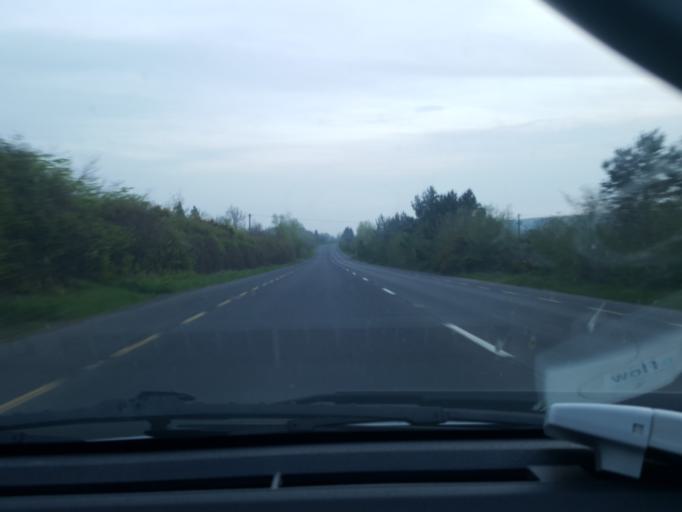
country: IE
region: Munster
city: Cahir
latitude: 52.3611
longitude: -7.9813
